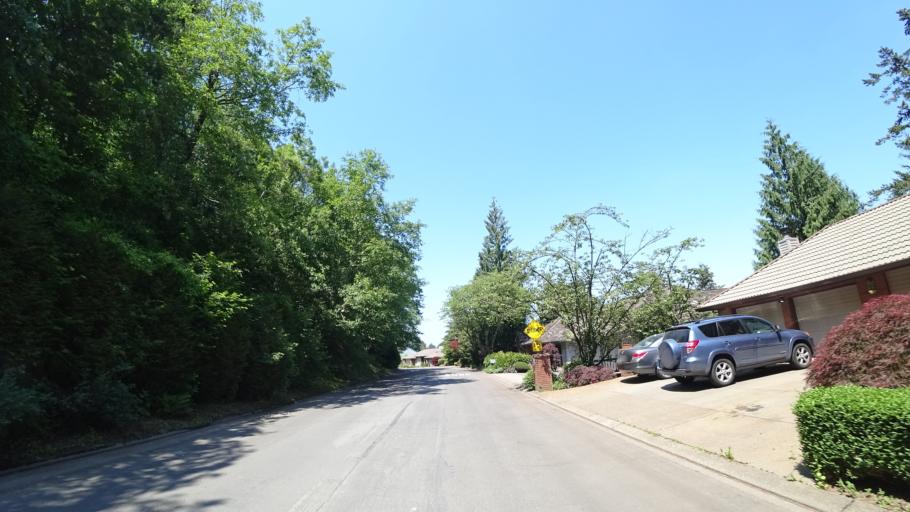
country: US
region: Oregon
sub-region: Washington County
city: Metzger
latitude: 45.4384
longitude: -122.7193
